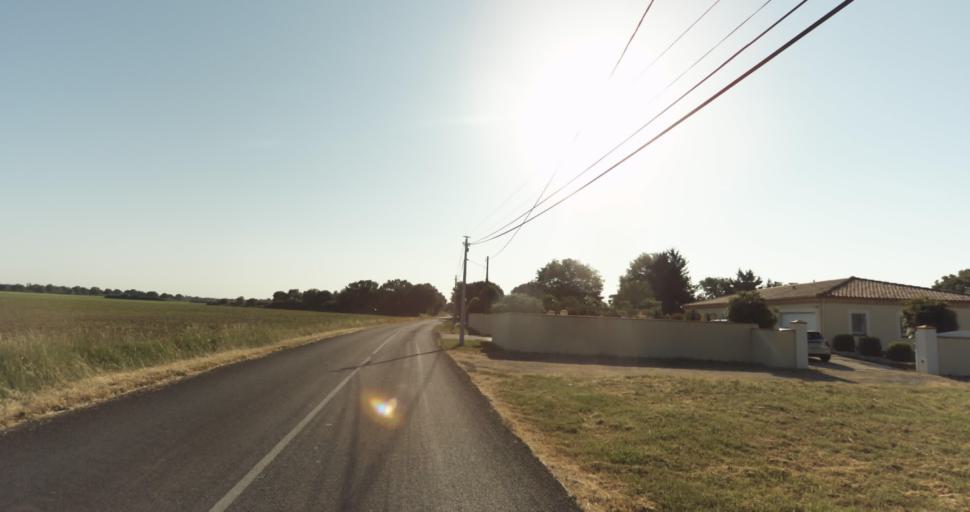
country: FR
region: Midi-Pyrenees
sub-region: Departement de la Haute-Garonne
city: Fontenilles
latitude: 43.5660
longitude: 1.2201
